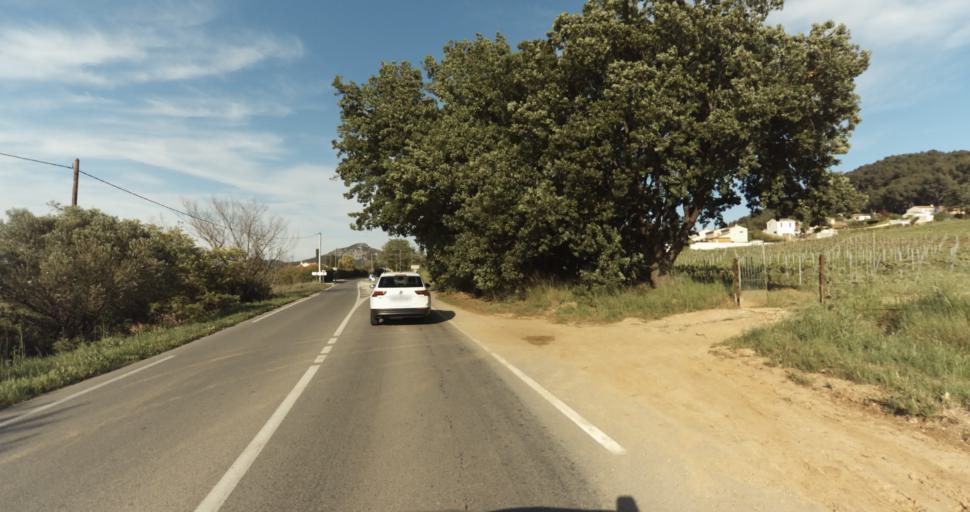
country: FR
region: Provence-Alpes-Cote d'Azur
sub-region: Departement du Var
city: Carqueiranne
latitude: 43.1182
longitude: 6.0625
